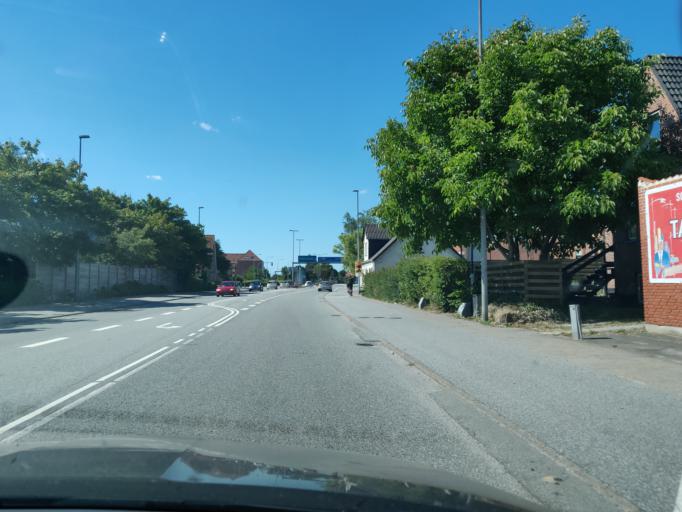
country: DK
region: North Denmark
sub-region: Alborg Kommune
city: Aalborg
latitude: 57.0711
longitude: 9.9480
